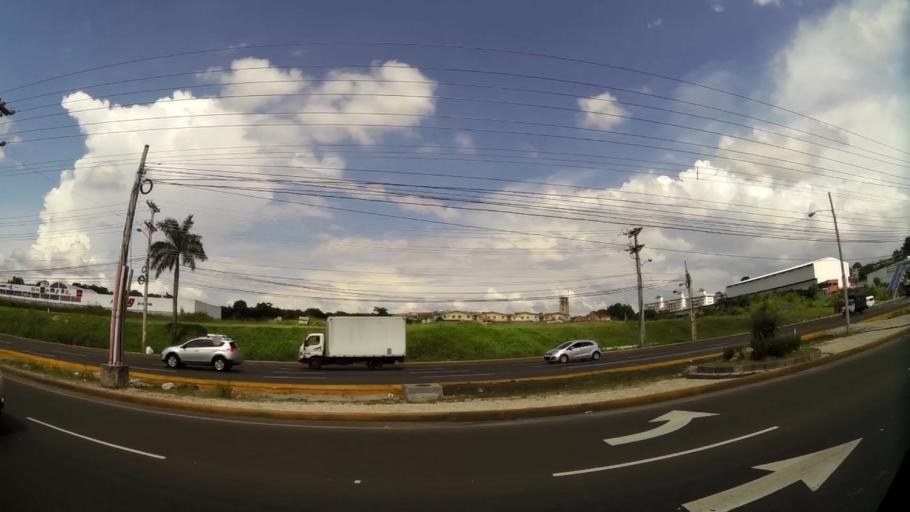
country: PA
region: Panama
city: San Miguelito
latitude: 9.0406
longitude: -79.4762
